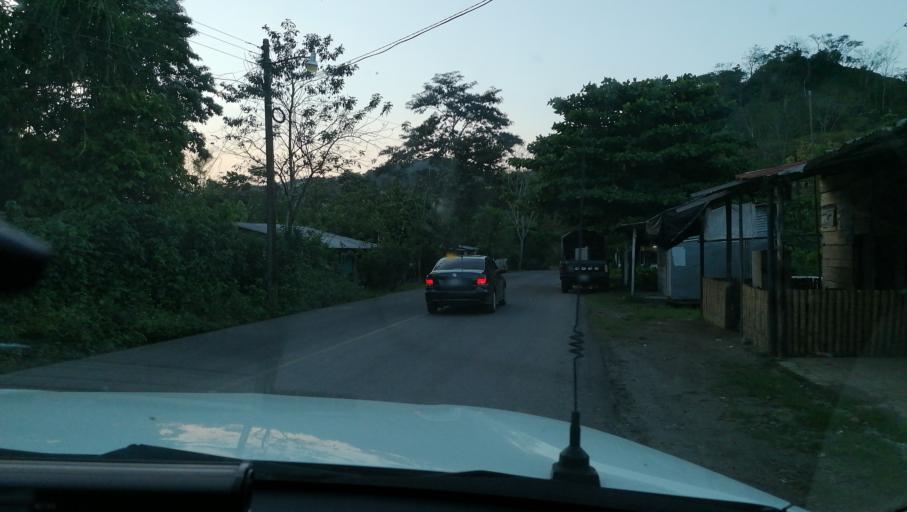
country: MX
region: Chiapas
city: Ostuacan
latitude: 17.4149
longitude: -93.3380
